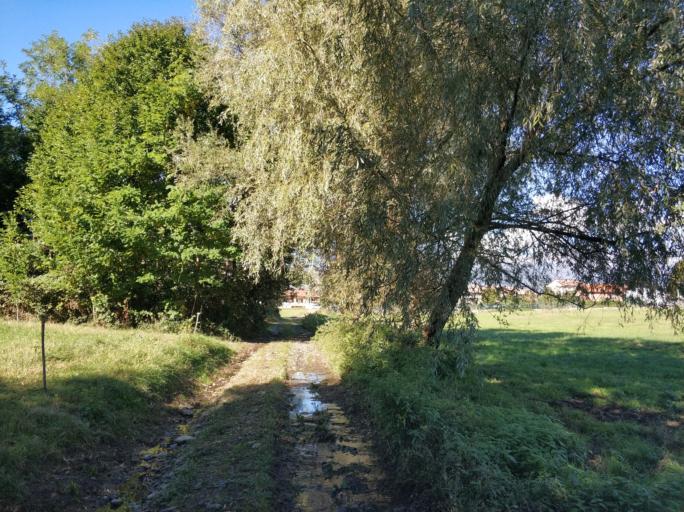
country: IT
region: Piedmont
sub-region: Provincia di Torino
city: Rocca Canavese
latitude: 45.2789
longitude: 7.5838
